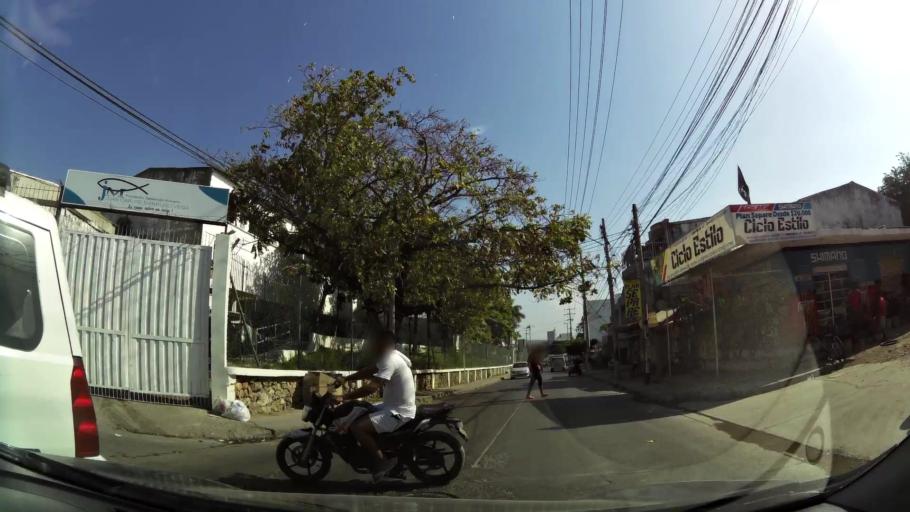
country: CO
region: Bolivar
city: Cartagena
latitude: 10.3949
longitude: -75.5043
